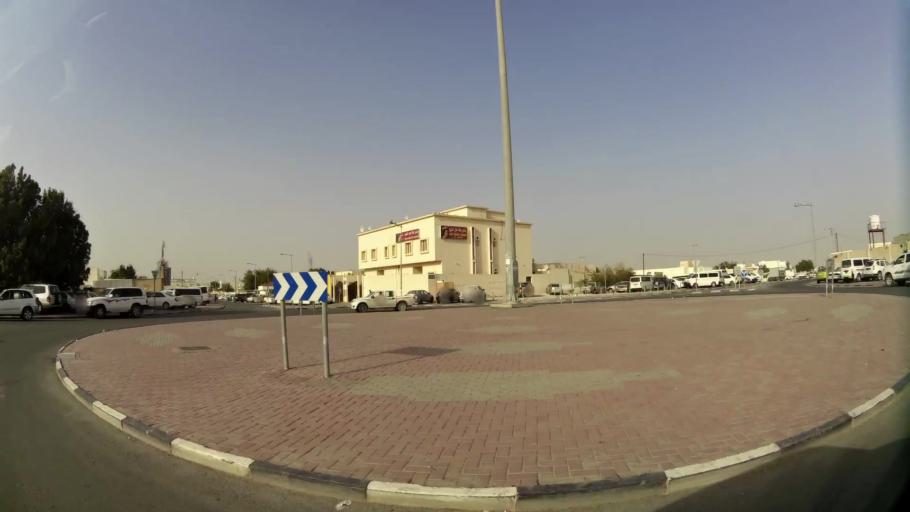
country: QA
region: Baladiyat ar Rayyan
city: Ar Rayyan
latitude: 25.2334
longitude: 51.4342
